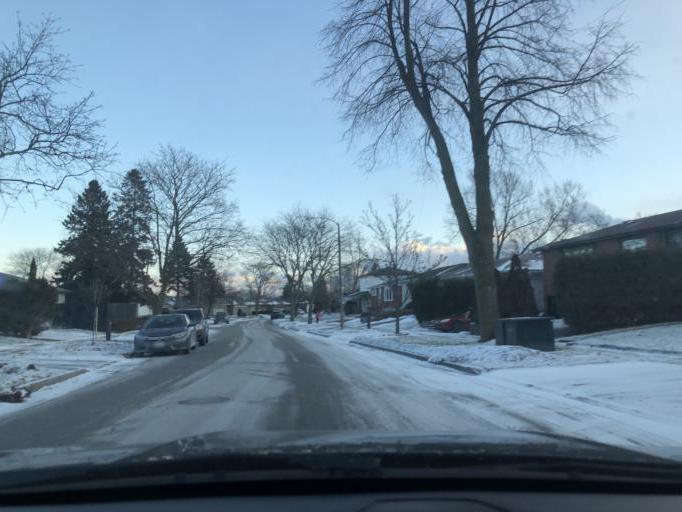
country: CA
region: Ontario
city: Pickering
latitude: 43.7876
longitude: -79.1432
